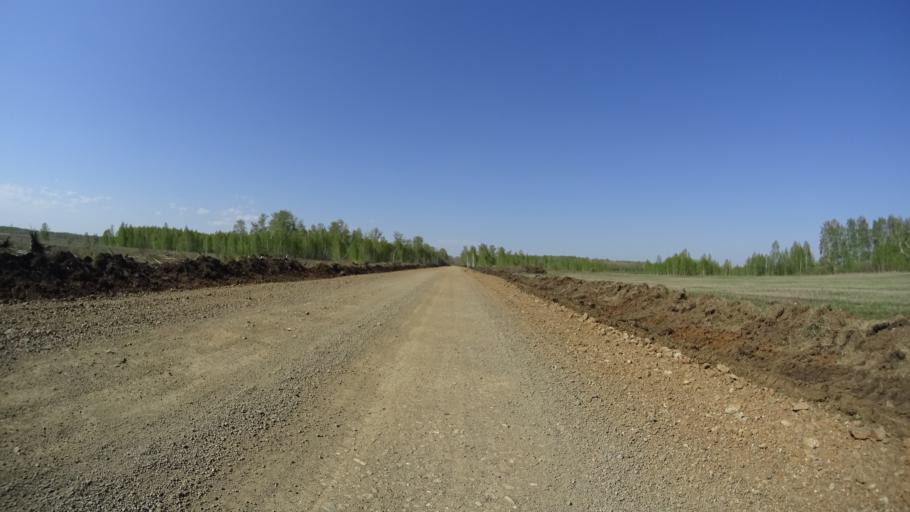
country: RU
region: Chelyabinsk
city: Troitsk
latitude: 54.1797
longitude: 61.4725
